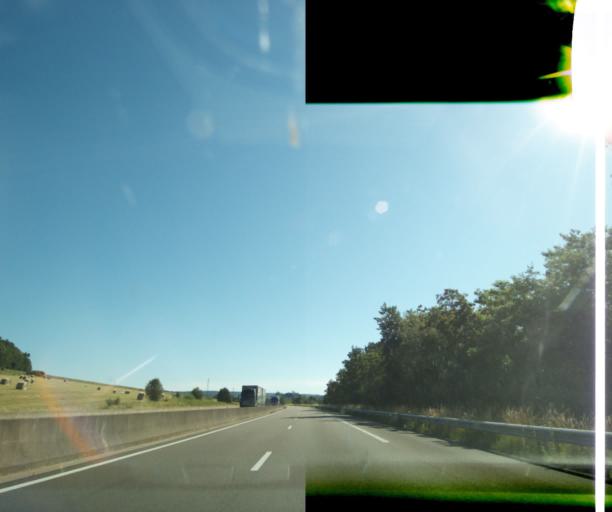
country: FR
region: Champagne-Ardenne
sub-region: Departement de la Haute-Marne
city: Rolampont
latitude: 47.9254
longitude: 5.2804
